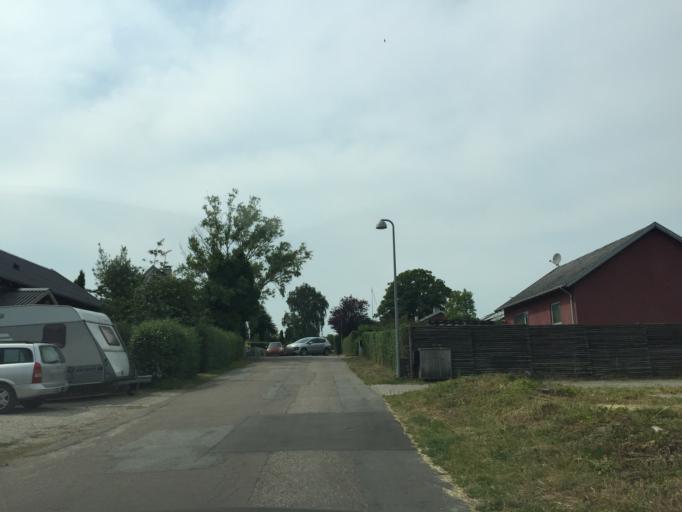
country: DK
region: Capital Region
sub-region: Hoje-Taastrup Kommune
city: Flong
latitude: 55.6531
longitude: 12.1906
